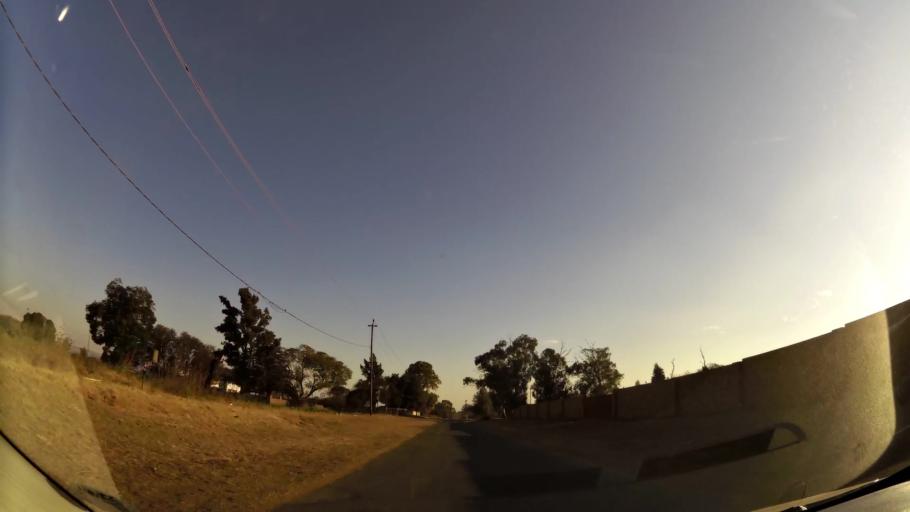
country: ZA
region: Gauteng
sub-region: West Rand District Municipality
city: Randfontein
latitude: -26.2152
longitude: 27.6548
